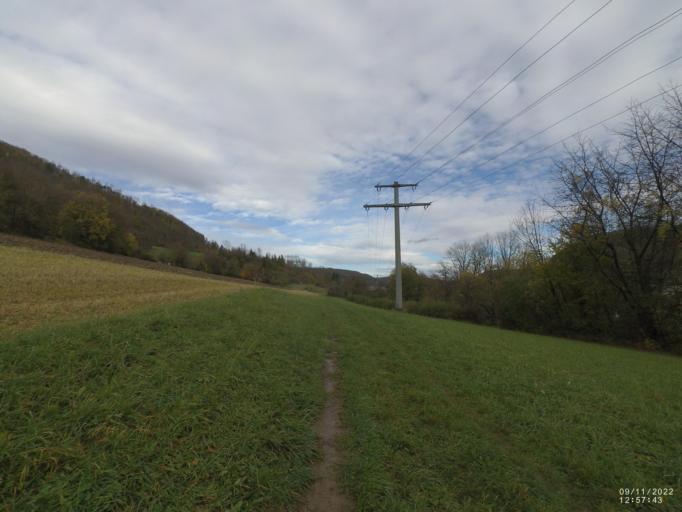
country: DE
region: Baden-Wuerttemberg
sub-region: Regierungsbezirk Stuttgart
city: Bad Uberkingen
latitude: 48.6133
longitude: 9.8050
